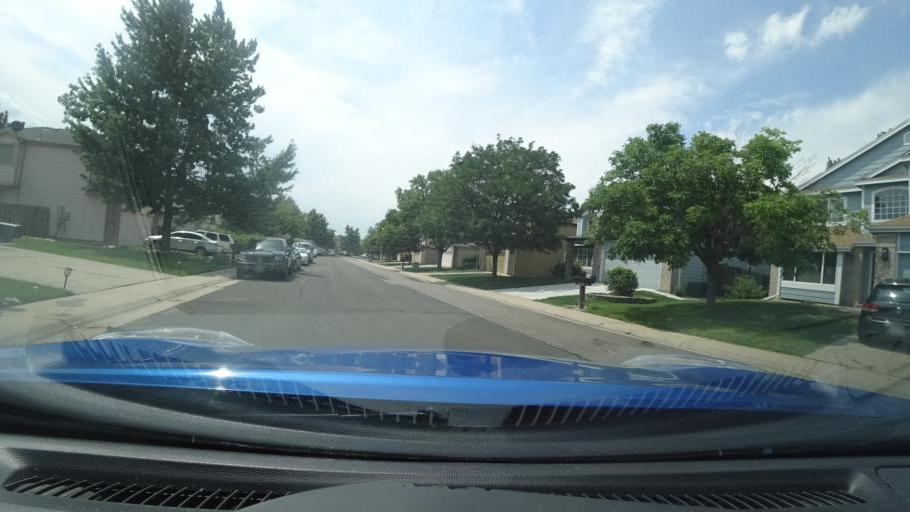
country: US
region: Colorado
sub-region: Adams County
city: Aurora
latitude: 39.6695
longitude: -104.7734
